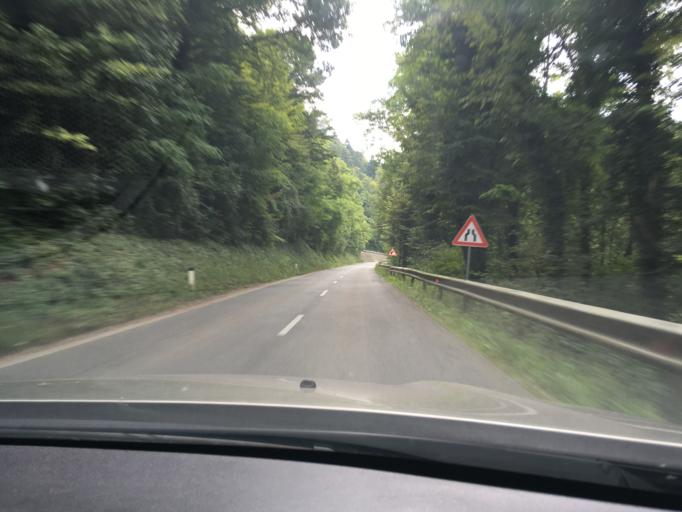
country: SI
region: Dolenjske Toplice
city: Dolenjske Toplice
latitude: 45.7642
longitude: 15.0561
